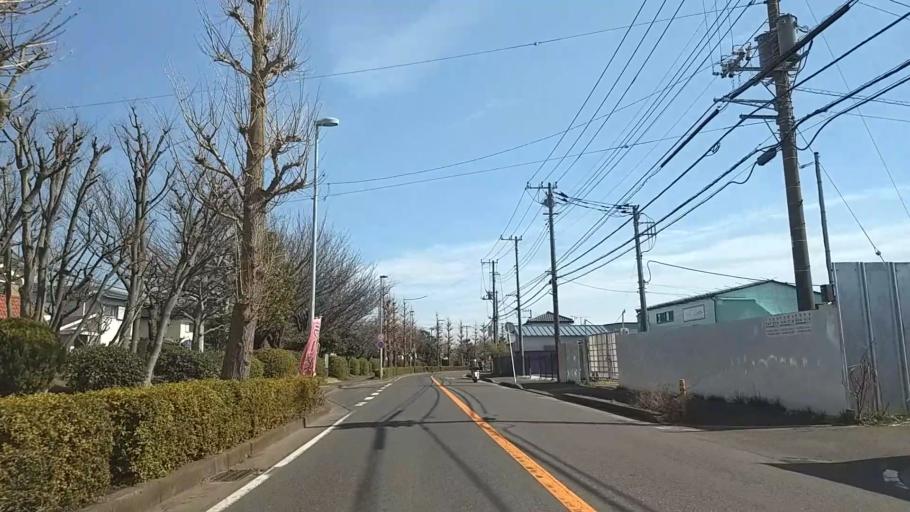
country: JP
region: Kanagawa
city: Fujisawa
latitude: 35.3670
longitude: 139.4337
